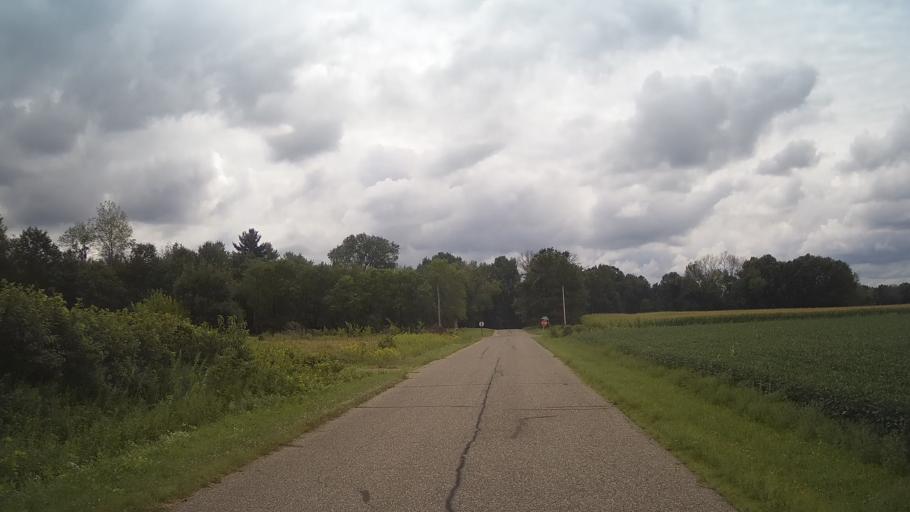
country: US
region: Wisconsin
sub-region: Adams County
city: Friendship
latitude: 44.0260
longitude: -89.9177
